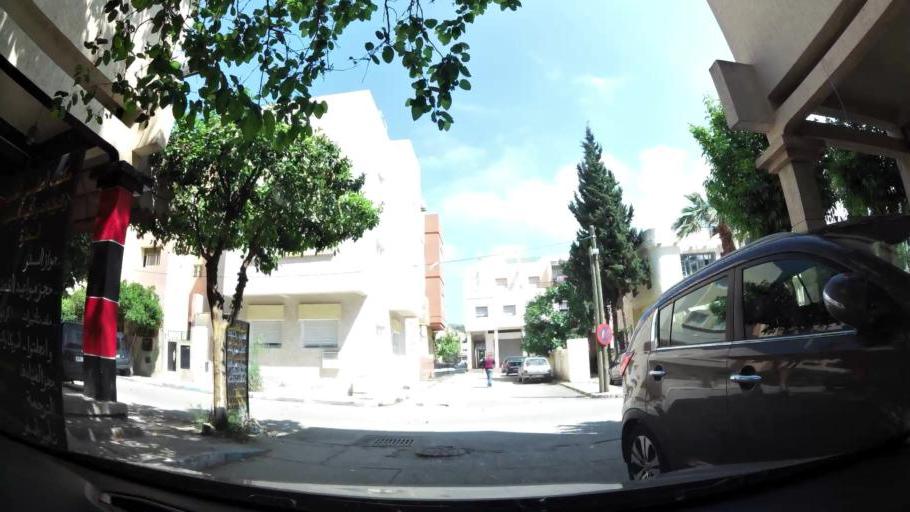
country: MA
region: Fes-Boulemane
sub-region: Fes
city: Fes
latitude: 34.0553
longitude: -5.0346
